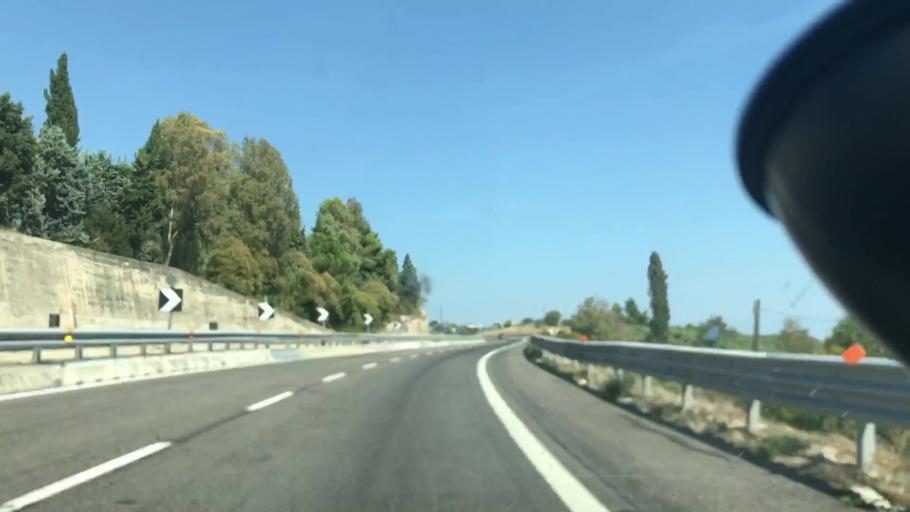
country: IT
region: Abruzzo
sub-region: Provincia di Chieti
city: Marina di Vasto
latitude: 42.0877
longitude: 14.6975
